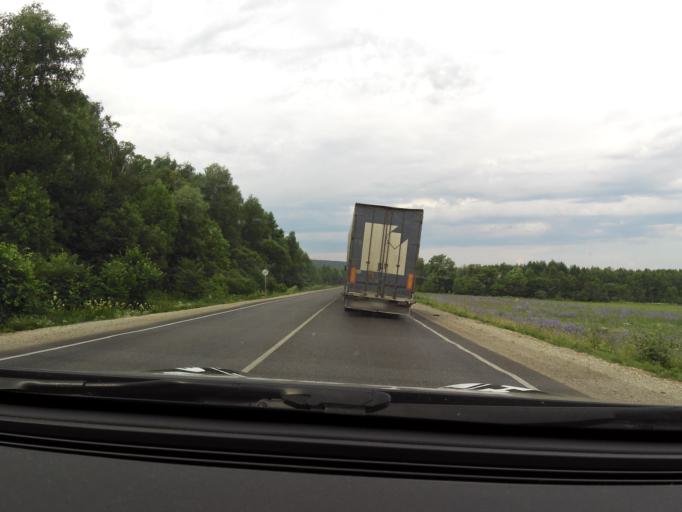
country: RU
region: Bashkortostan
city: Ulu-Telyak
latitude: 54.8495
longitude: 57.1122
